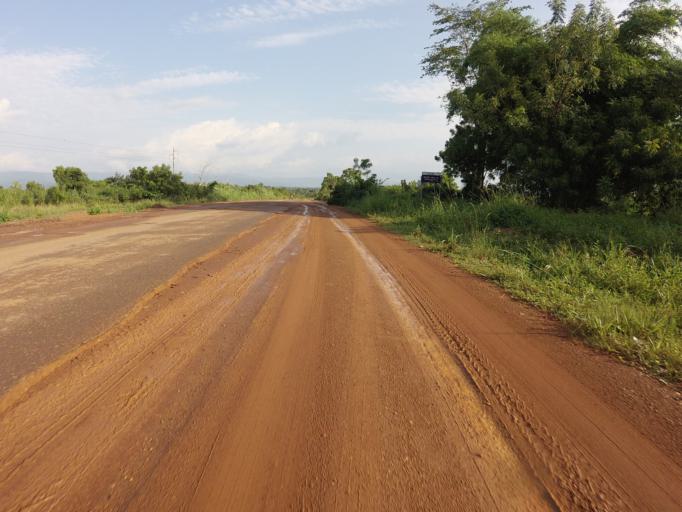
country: GH
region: Volta
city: Kpandu
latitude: 7.0195
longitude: 0.4281
